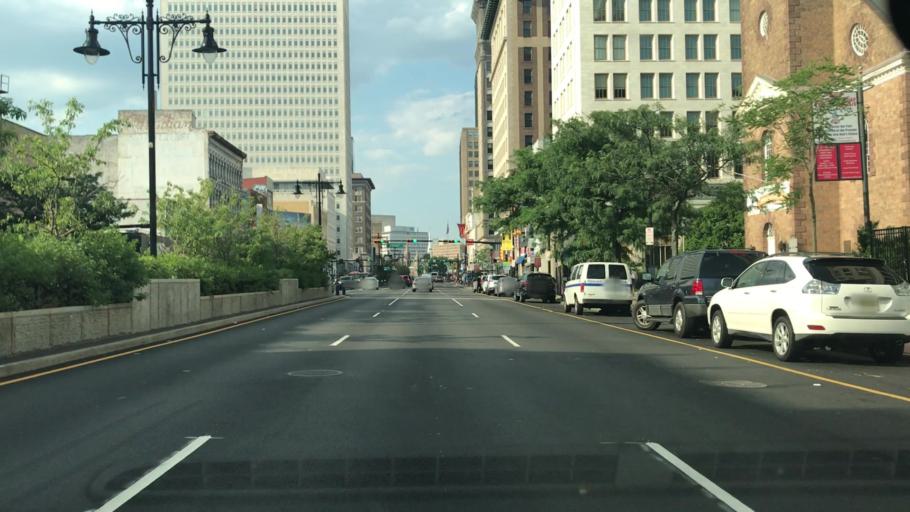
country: US
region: New Jersey
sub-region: Essex County
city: Newark
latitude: 40.7341
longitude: -74.1729
